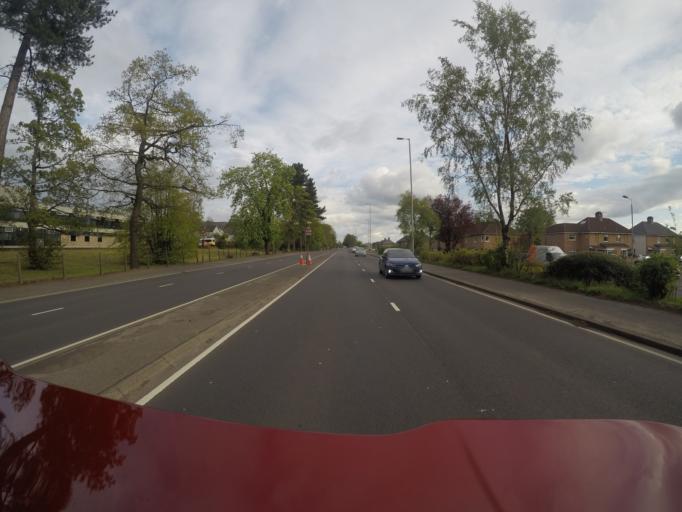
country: GB
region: Scotland
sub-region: West Dunbartonshire
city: Dumbarton
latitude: 55.9475
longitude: -4.5478
